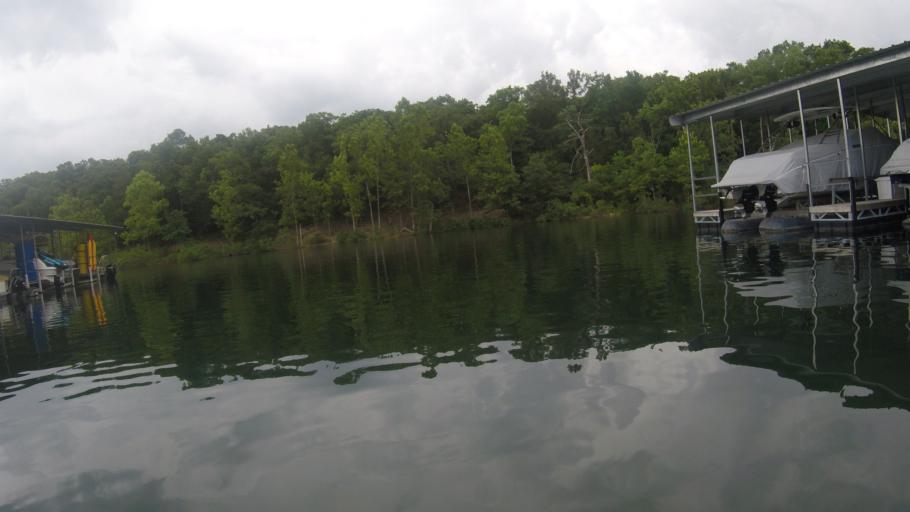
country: US
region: Missouri
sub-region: Barry County
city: Shell Knob
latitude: 36.5943
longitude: -93.5498
